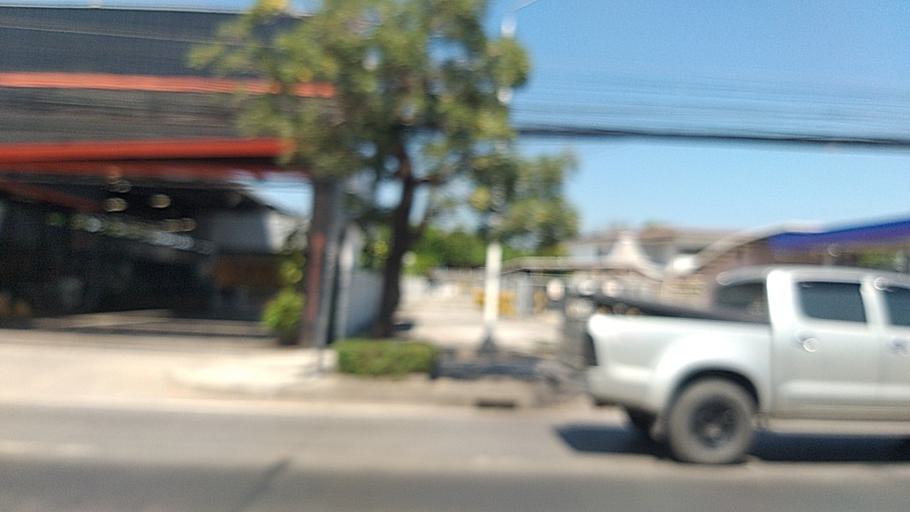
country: TH
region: Nakhon Ratchasima
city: Nakhon Ratchasima
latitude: 14.9796
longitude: 102.0834
